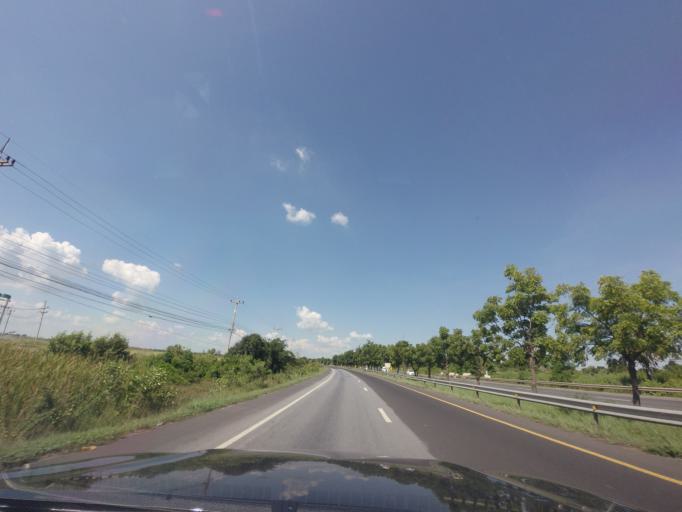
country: TH
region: Nakhon Ratchasima
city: Non Sung
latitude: 15.1913
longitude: 102.3472
